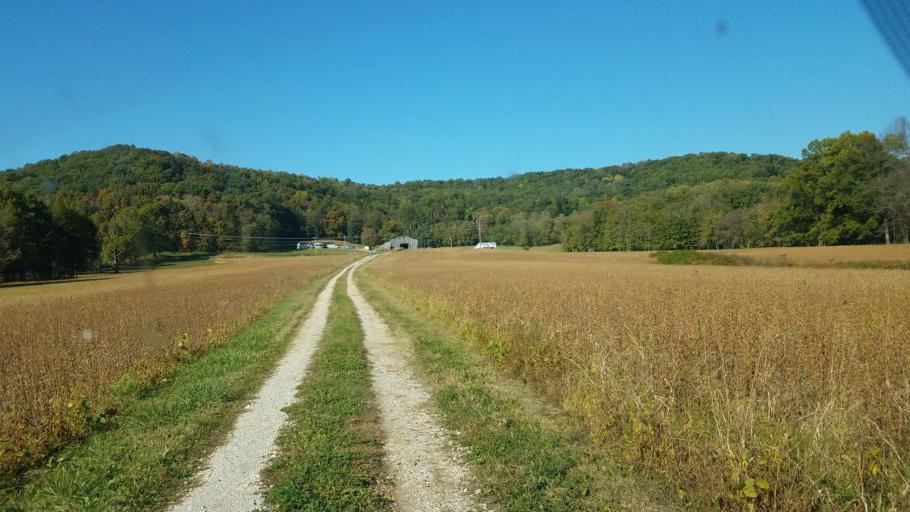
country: US
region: Kentucky
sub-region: Fleming County
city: Flemingsburg
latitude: 38.4645
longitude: -83.5610
